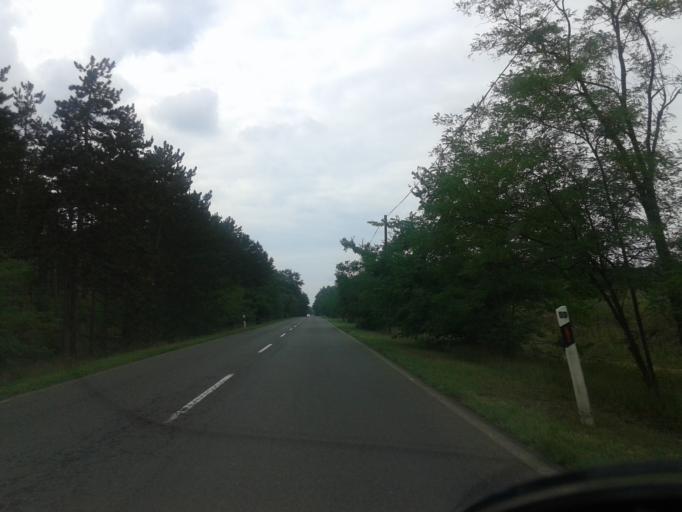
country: HU
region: Csongrad
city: Asotthalom
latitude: 46.2189
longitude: 19.7760
